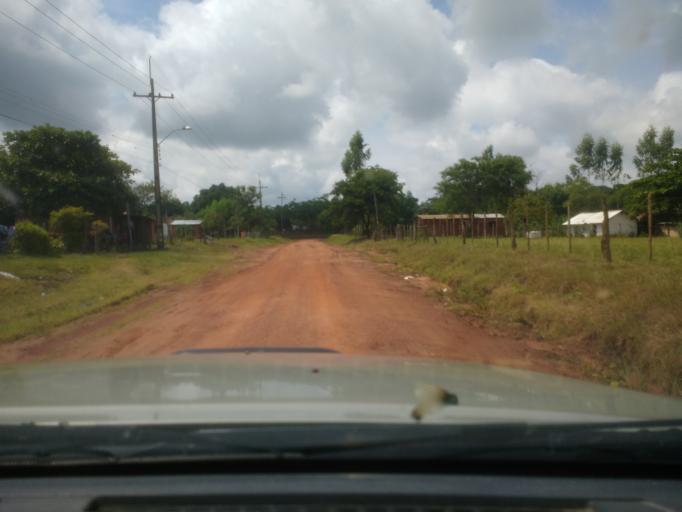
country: PY
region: San Pedro
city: Puerto Rosario
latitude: -24.4101
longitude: -57.1029
